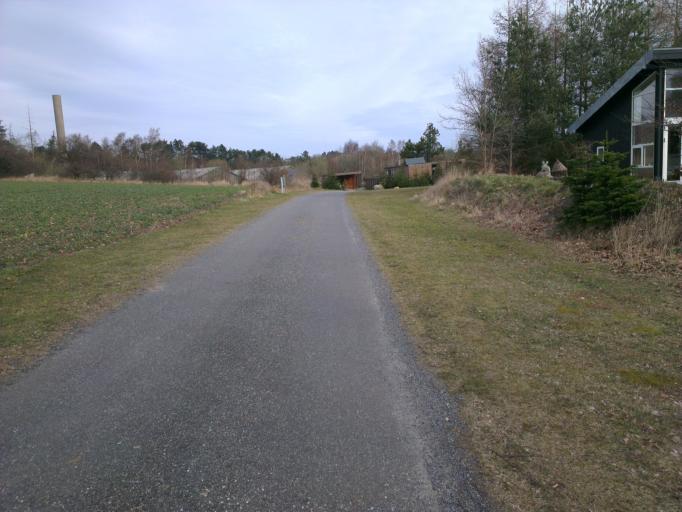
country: DK
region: Capital Region
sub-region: Frederikssund Kommune
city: Frederikssund
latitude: 55.8242
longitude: 12.0320
